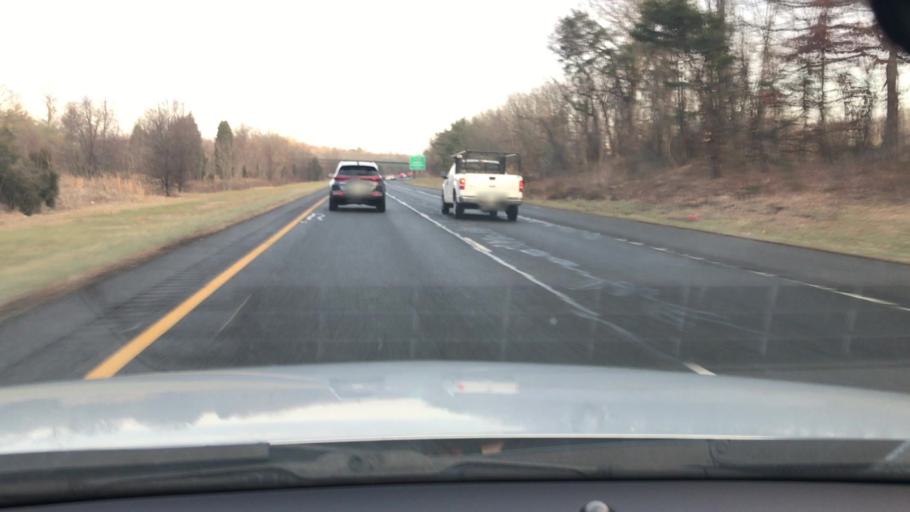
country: US
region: New Jersey
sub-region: Camden County
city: Blackwood
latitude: 39.8101
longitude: -75.1052
